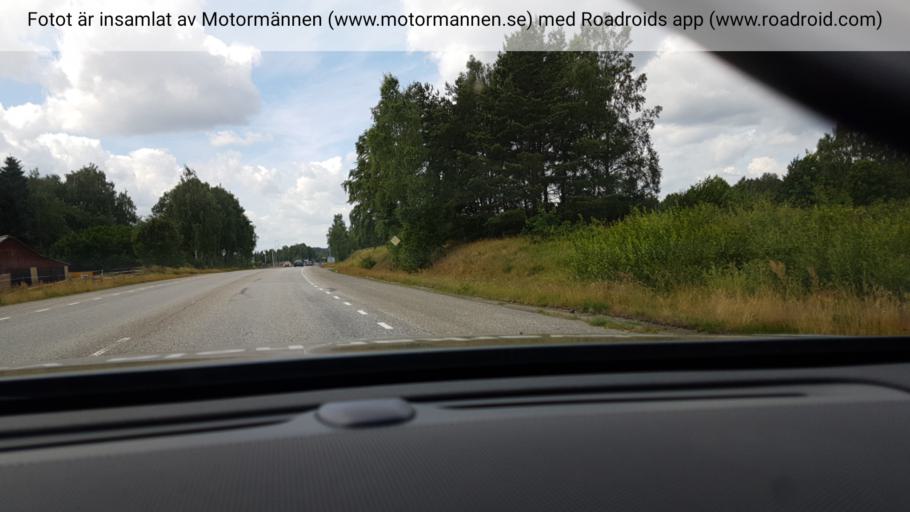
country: SE
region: Skane
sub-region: Hassleholms Kommun
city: Hassleholm
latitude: 56.1699
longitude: 13.8078
